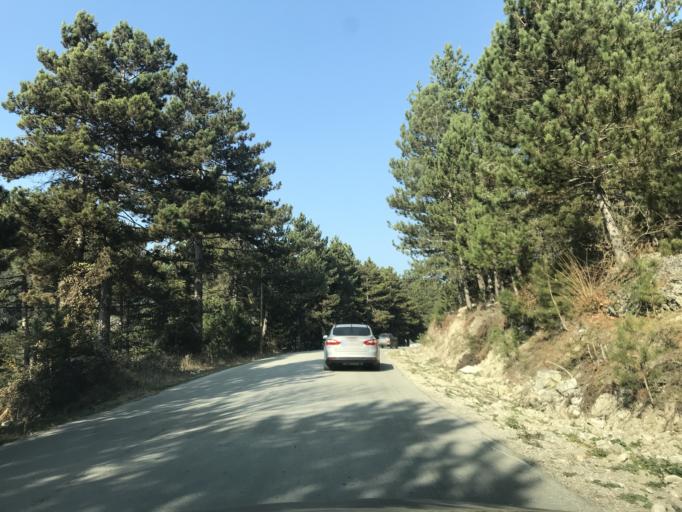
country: TR
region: Bolu
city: Bolu
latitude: 40.7843
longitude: 31.6327
